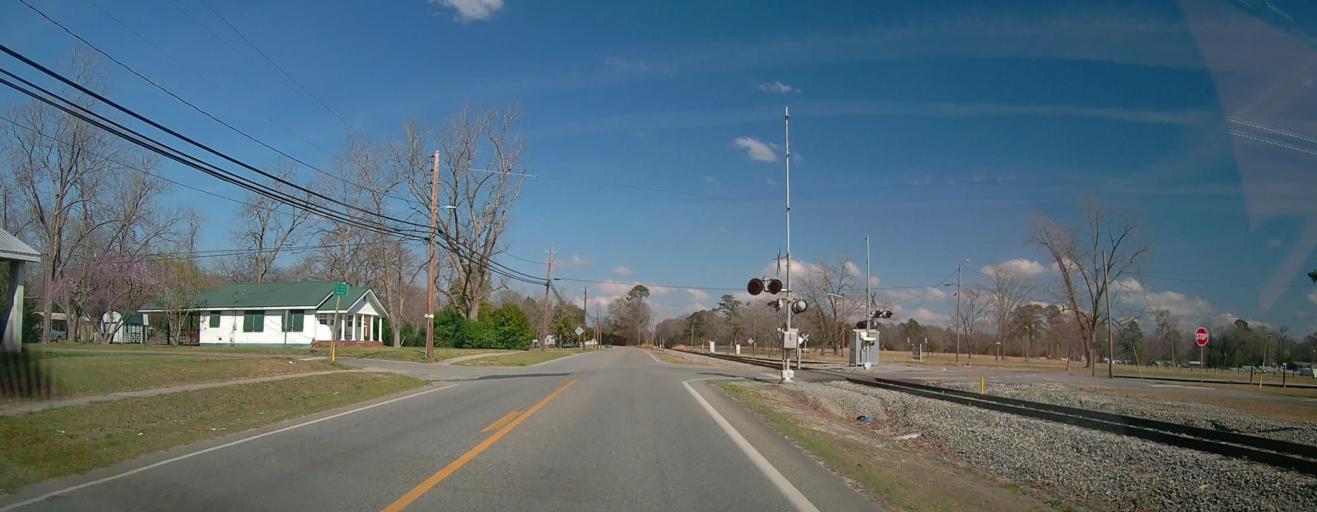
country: US
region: Georgia
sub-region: Wilkinson County
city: Gordon
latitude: 32.8836
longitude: -83.3259
